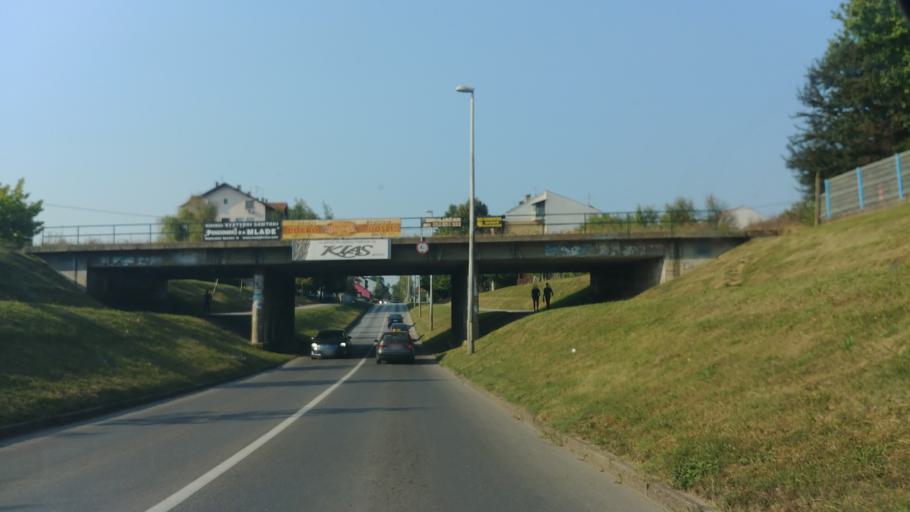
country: BA
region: Brcko
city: Brcko
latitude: 44.8651
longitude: 18.8112
